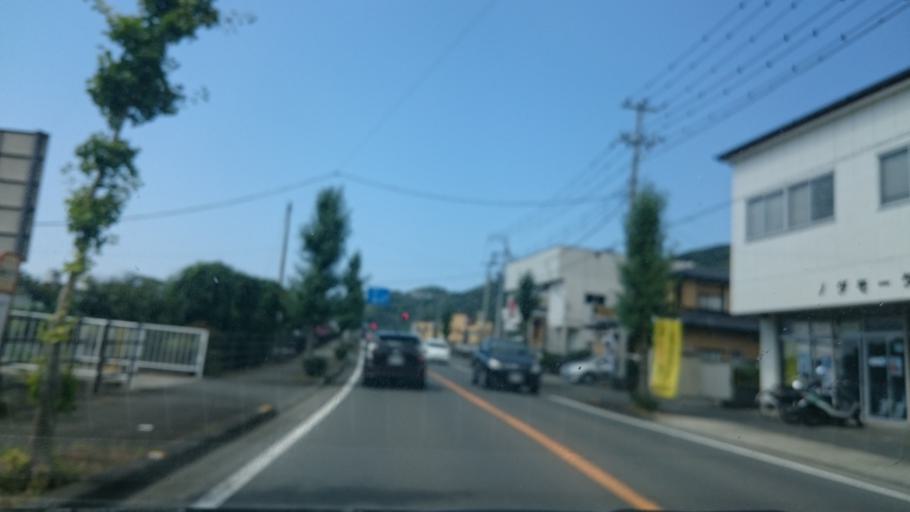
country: JP
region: Shizuoka
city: Shimoda
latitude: 34.7526
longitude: 138.7819
